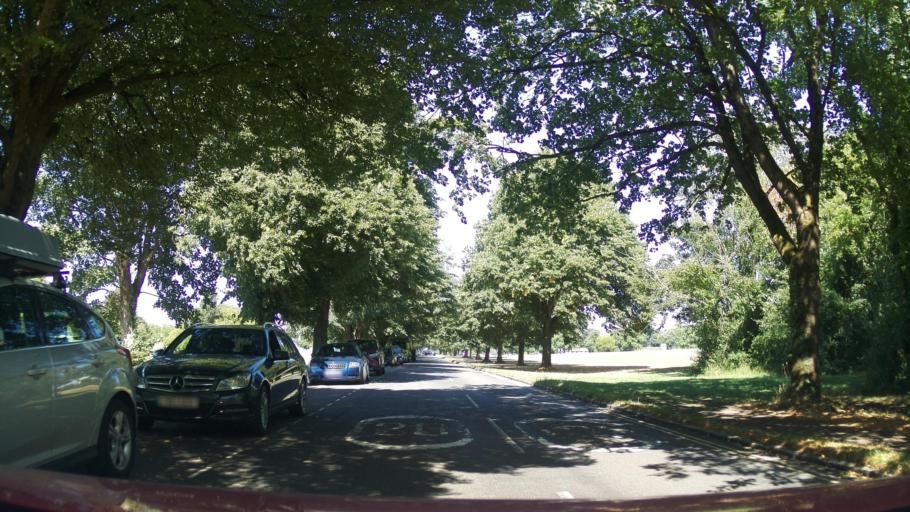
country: GB
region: England
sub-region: Bristol
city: Bristol
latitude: 51.4692
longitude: -2.6233
